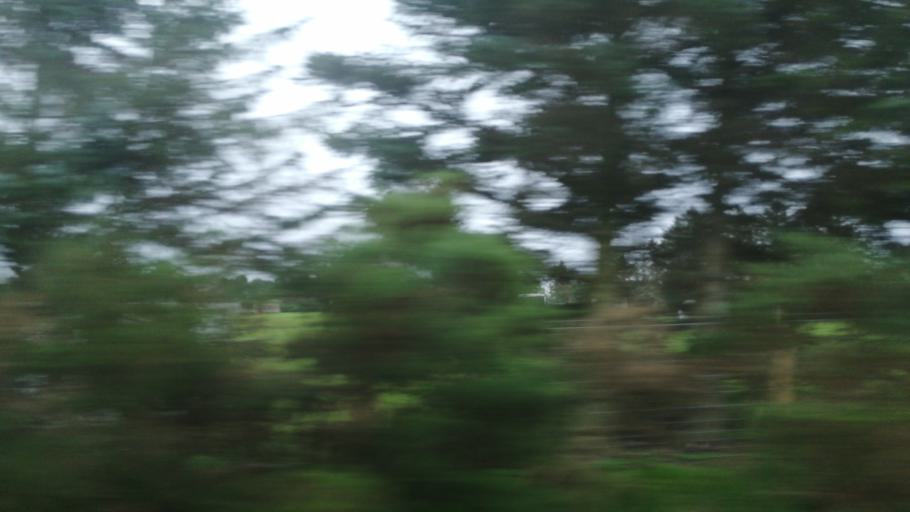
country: GB
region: Scotland
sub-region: Highland
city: Brora
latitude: 58.0289
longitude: -3.8487
